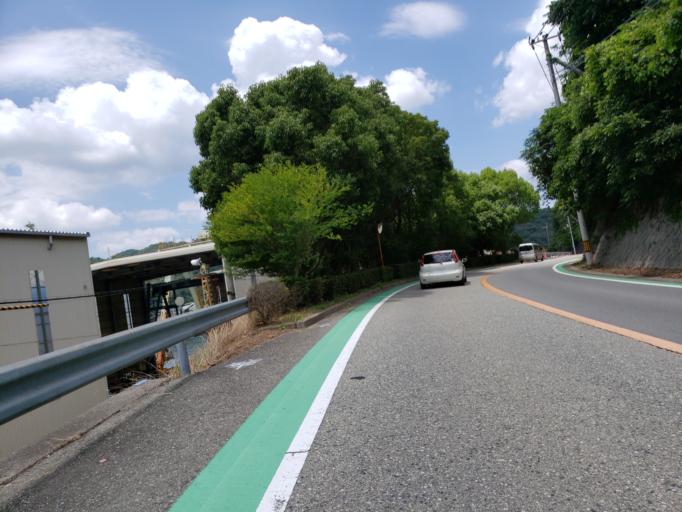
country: JP
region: Hyogo
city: Aioi
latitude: 34.7915
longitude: 134.4695
